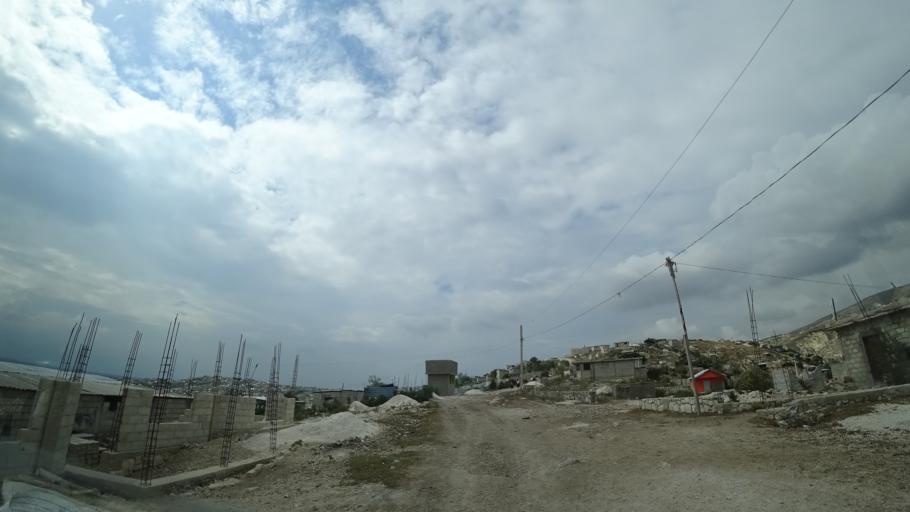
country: HT
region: Ouest
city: Croix des Bouquets
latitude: 18.6641
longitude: -72.2602
